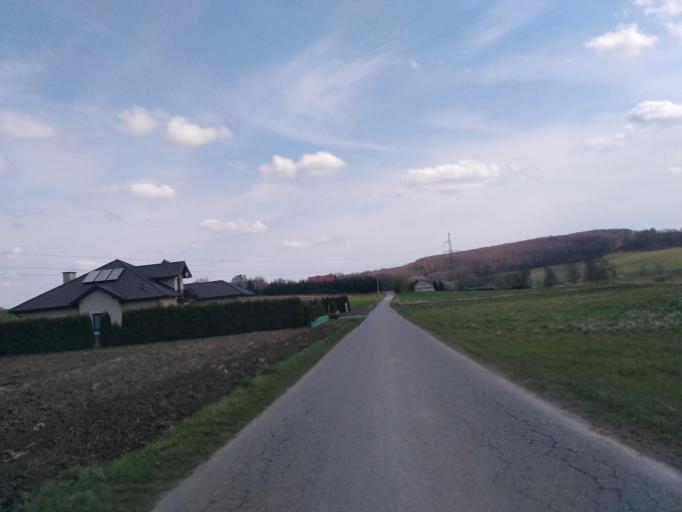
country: PL
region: Subcarpathian Voivodeship
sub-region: Powiat ropczycko-sedziszowski
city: Iwierzyce
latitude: 50.0461
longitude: 21.7377
